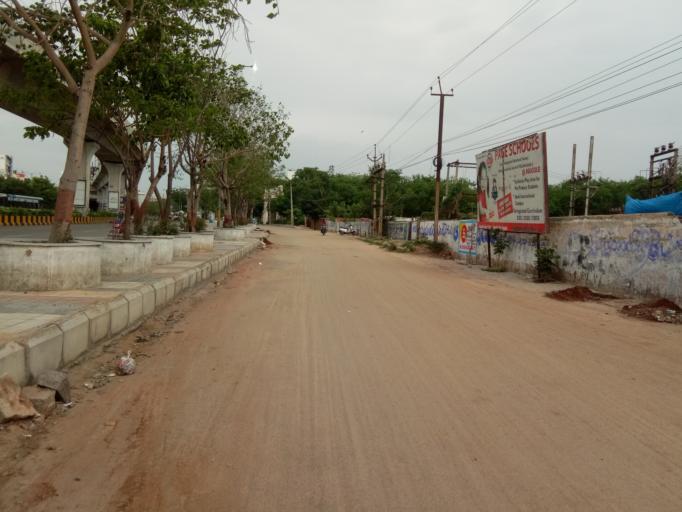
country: IN
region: Telangana
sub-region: Rangareddi
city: Lal Bahadur Nagar
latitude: 17.3522
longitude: 78.5464
